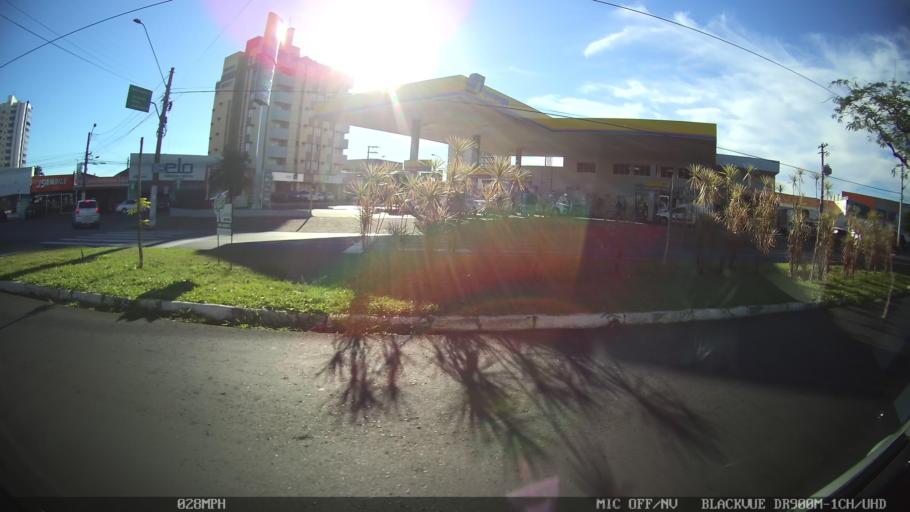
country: BR
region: Sao Paulo
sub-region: Araraquara
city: Araraquara
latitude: -21.7781
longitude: -48.1781
